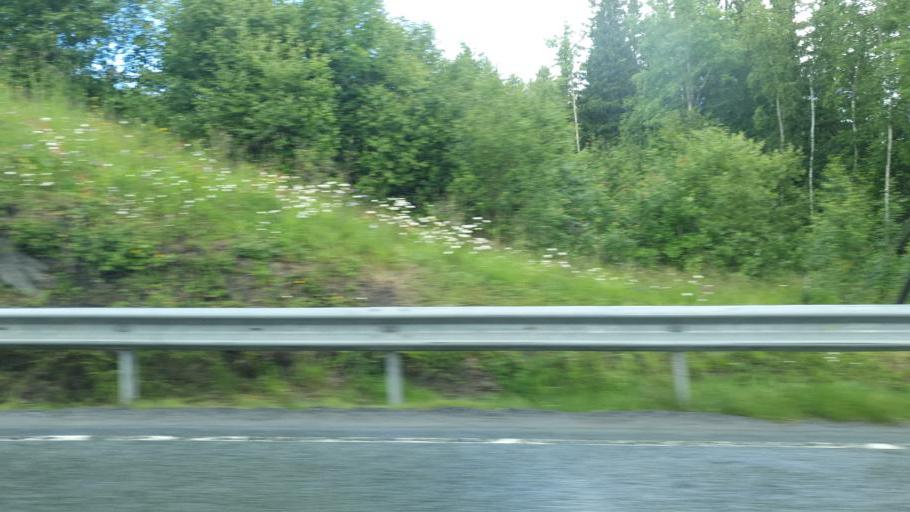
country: NO
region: Sor-Trondelag
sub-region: Rennebu
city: Berkak
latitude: 62.8160
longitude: 10.0313
